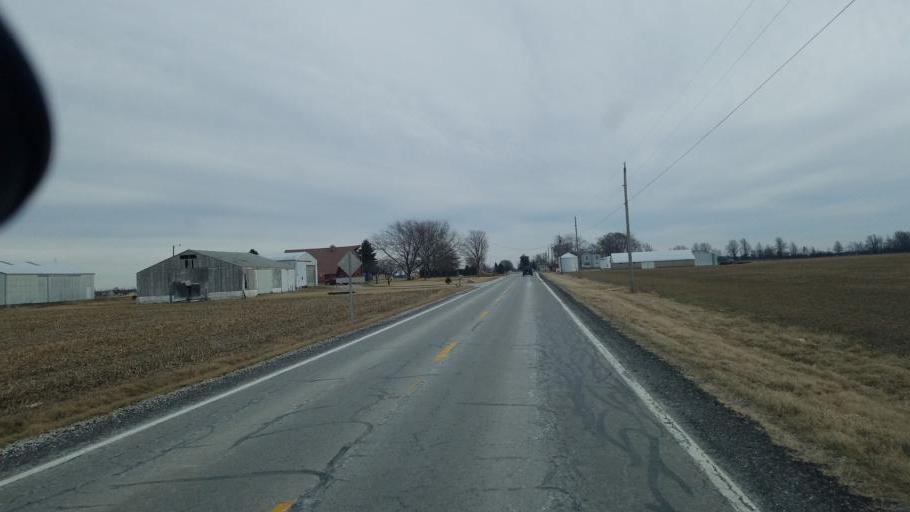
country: US
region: Ohio
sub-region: Marion County
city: Prospect
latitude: 40.4515
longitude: -83.1248
